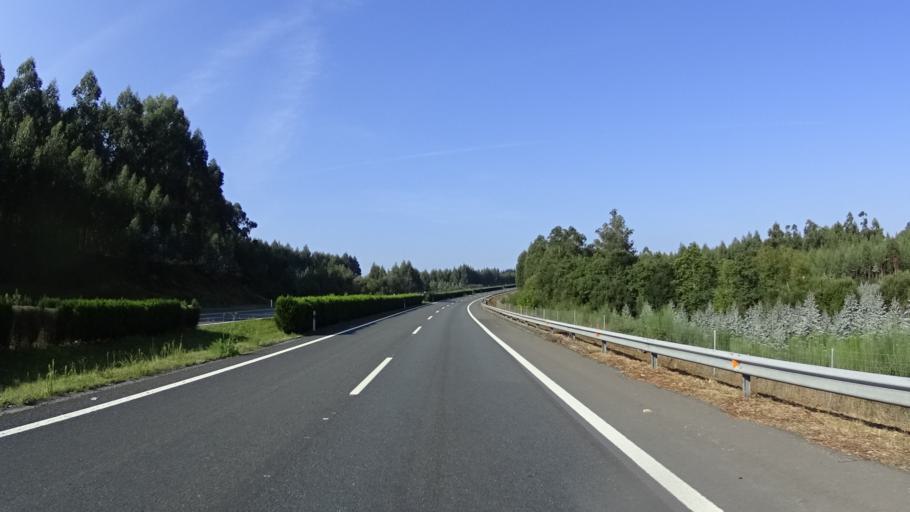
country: ES
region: Galicia
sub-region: Provincia da Coruna
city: Coiros
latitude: 43.2397
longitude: -8.1163
